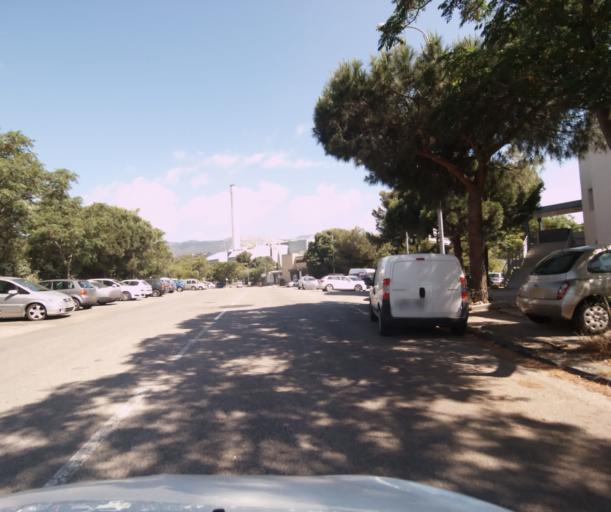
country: FR
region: Provence-Alpes-Cote d'Azur
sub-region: Departement du Var
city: La Seyne-sur-Mer
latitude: 43.1228
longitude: 5.8921
